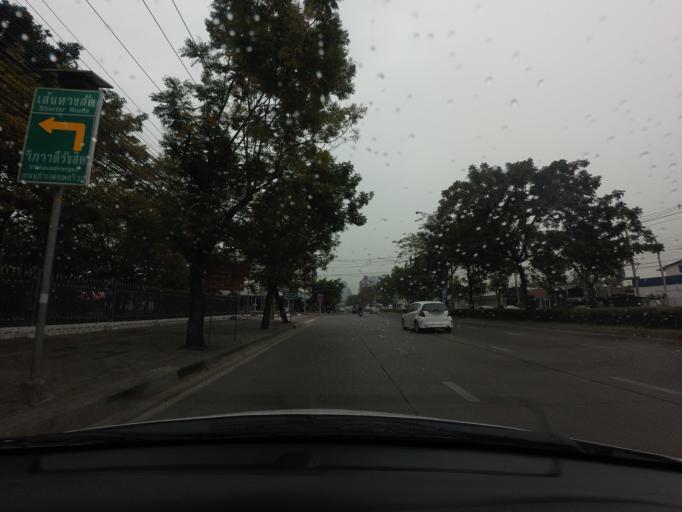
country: TH
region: Bangkok
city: Bang Sue
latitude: 13.8036
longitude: 100.5484
